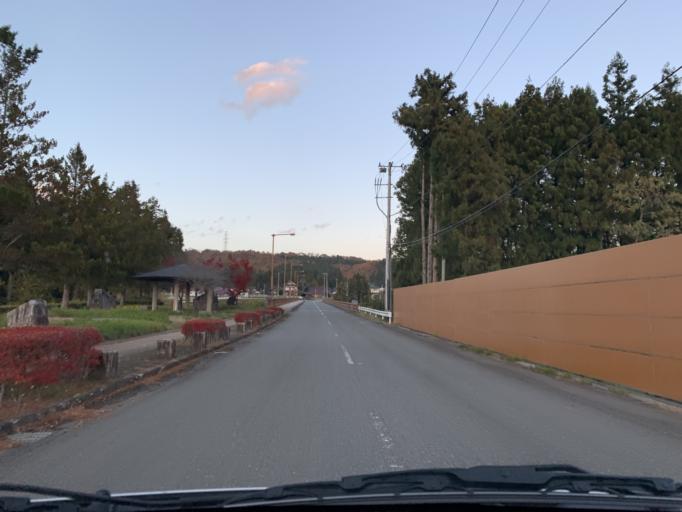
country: JP
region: Iwate
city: Ichinoseki
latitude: 39.0158
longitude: 141.0896
